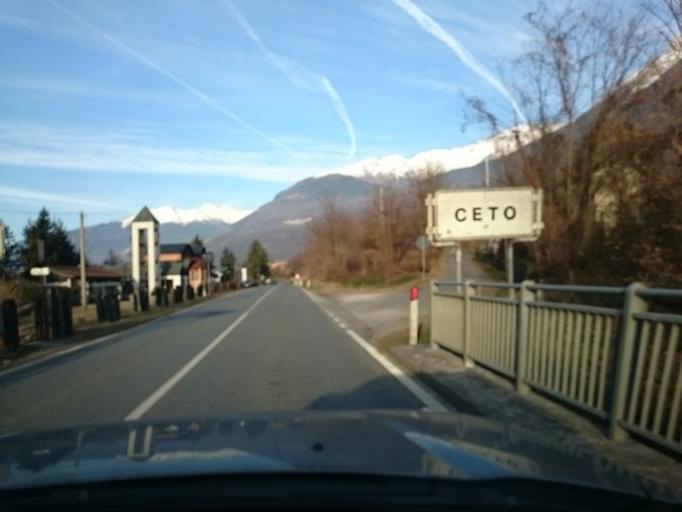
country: IT
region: Lombardy
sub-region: Provincia di Brescia
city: Braone
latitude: 45.9922
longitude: 10.3360
